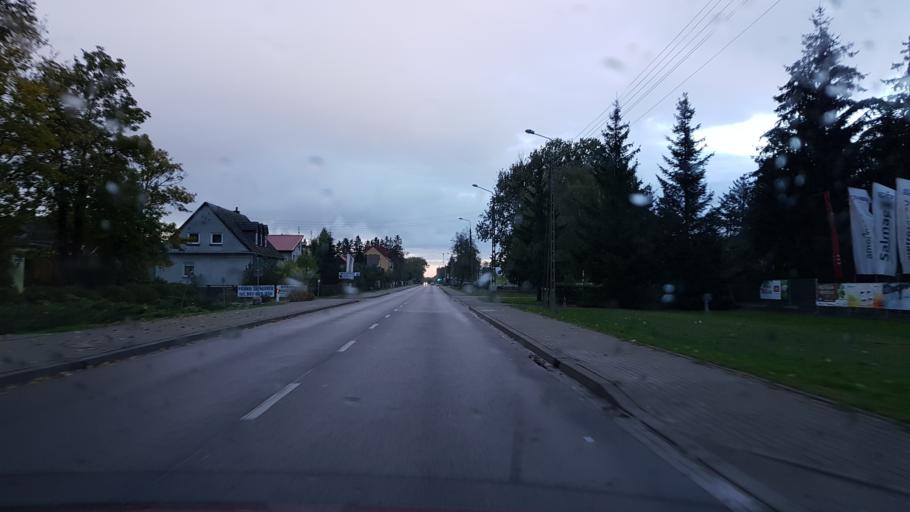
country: PL
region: Greater Poland Voivodeship
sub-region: Powiat zlotowski
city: Krajenka
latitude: 53.2891
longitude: 16.9834
